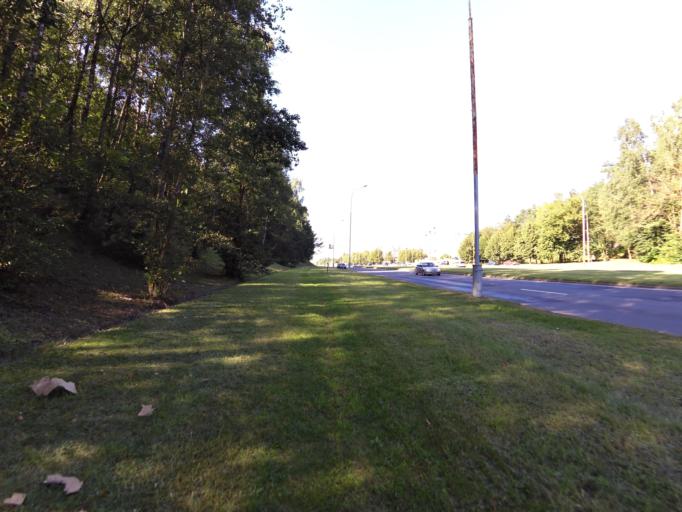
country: LT
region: Vilnius County
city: Seskine
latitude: 54.7252
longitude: 25.2688
